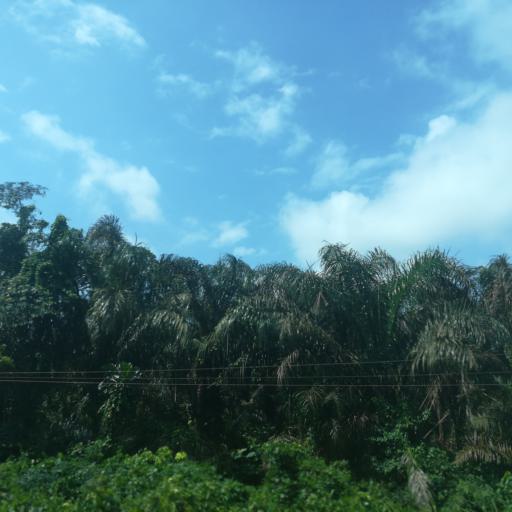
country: NG
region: Lagos
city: Ikorodu
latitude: 6.6566
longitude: 3.6888
